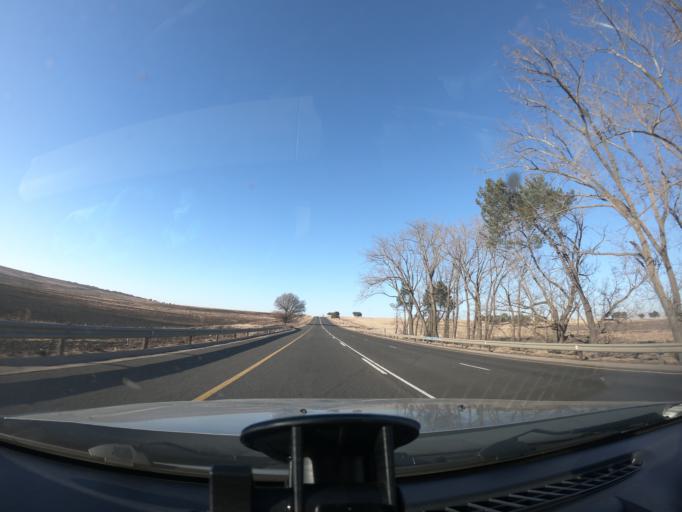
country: ZA
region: Mpumalanga
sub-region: Gert Sibande District Municipality
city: Ermelo
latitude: -26.4500
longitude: 29.9495
